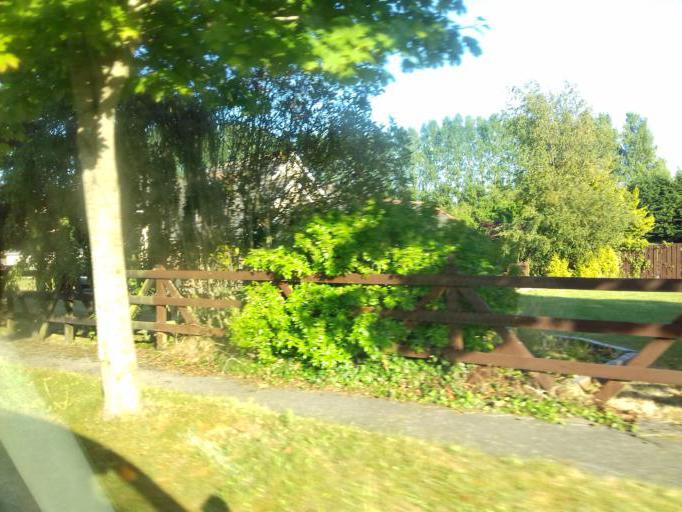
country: IE
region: Leinster
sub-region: Fingal County
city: Swords
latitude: 53.4875
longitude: -6.3043
